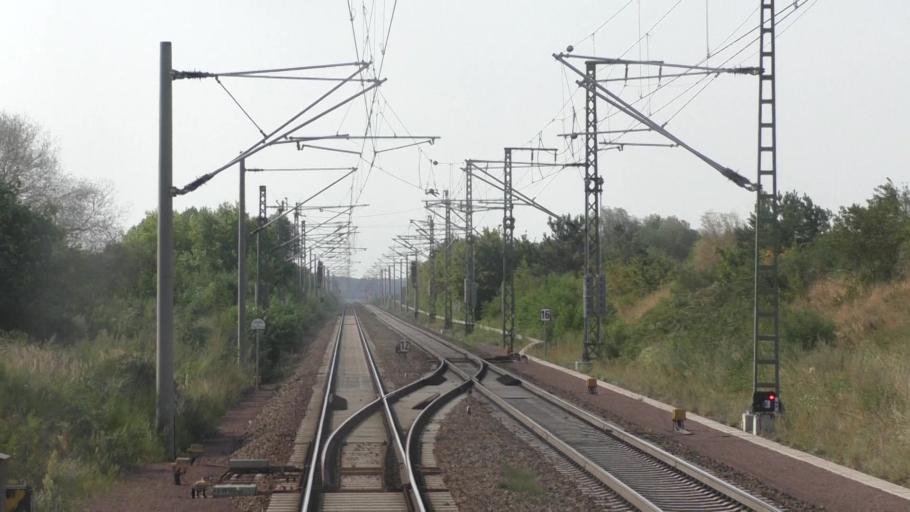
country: DE
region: Saxony-Anhalt
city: Rodleben
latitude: 51.8989
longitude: 12.2134
